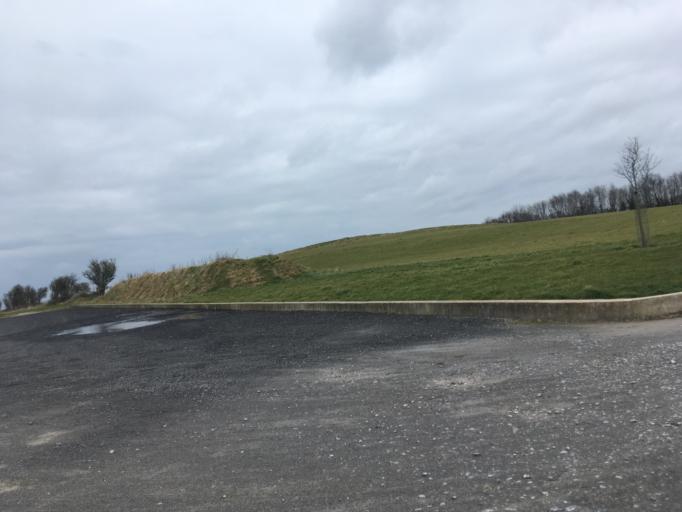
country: IE
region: Leinster
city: Portmarnock
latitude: 53.4403
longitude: -6.1345
